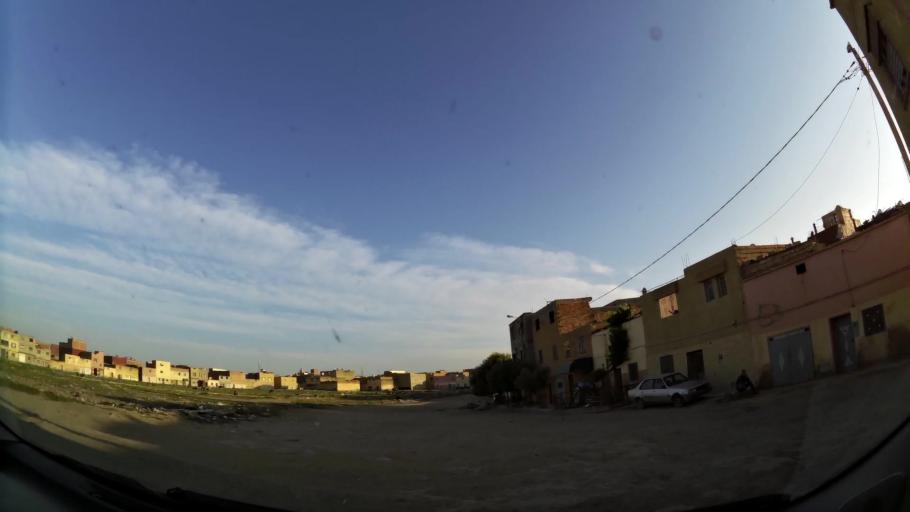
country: MA
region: Oriental
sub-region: Oujda-Angad
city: Oujda
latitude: 34.7055
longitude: -1.9090
